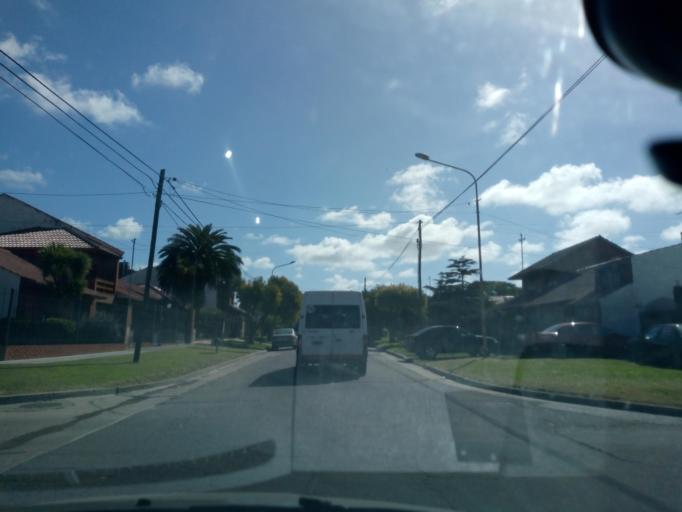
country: AR
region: Buenos Aires
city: Mar del Plata
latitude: -38.0517
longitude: -57.5571
